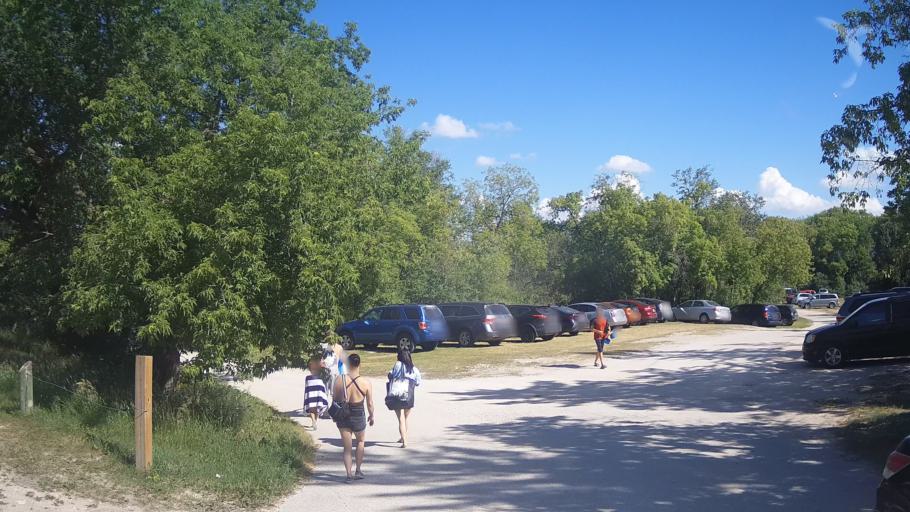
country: CA
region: Manitoba
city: Stonewall
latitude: 50.1420
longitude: -97.3278
